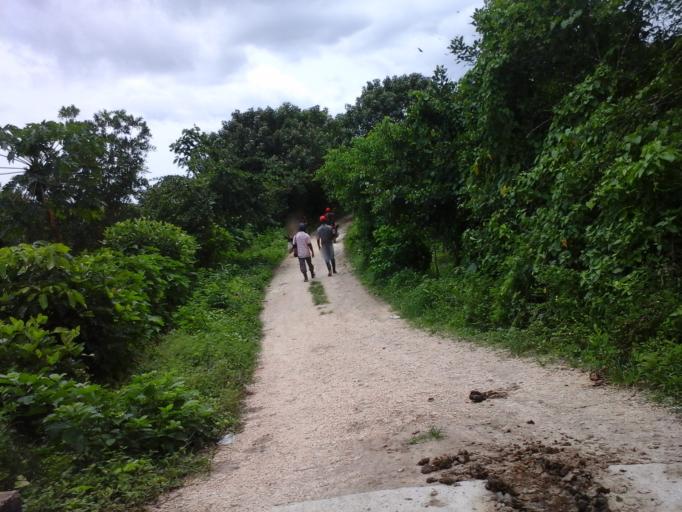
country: CO
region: Bolivar
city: San Pablo
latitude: 10.1511
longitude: -75.2764
